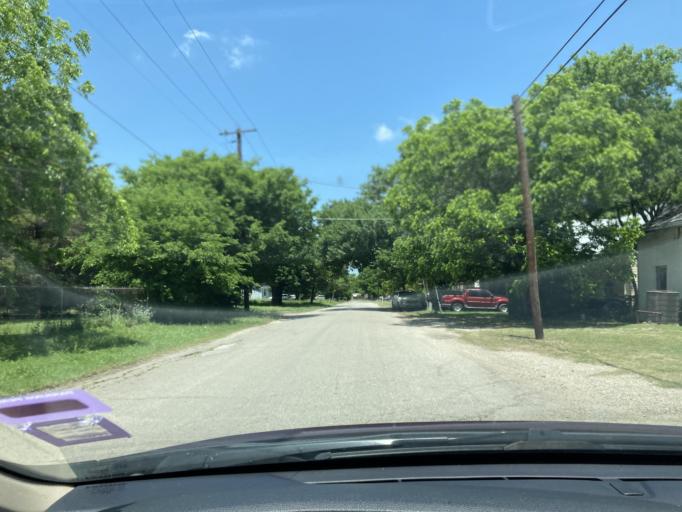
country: US
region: Texas
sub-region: Navarro County
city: Corsicana
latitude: 32.0819
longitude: -96.4658
